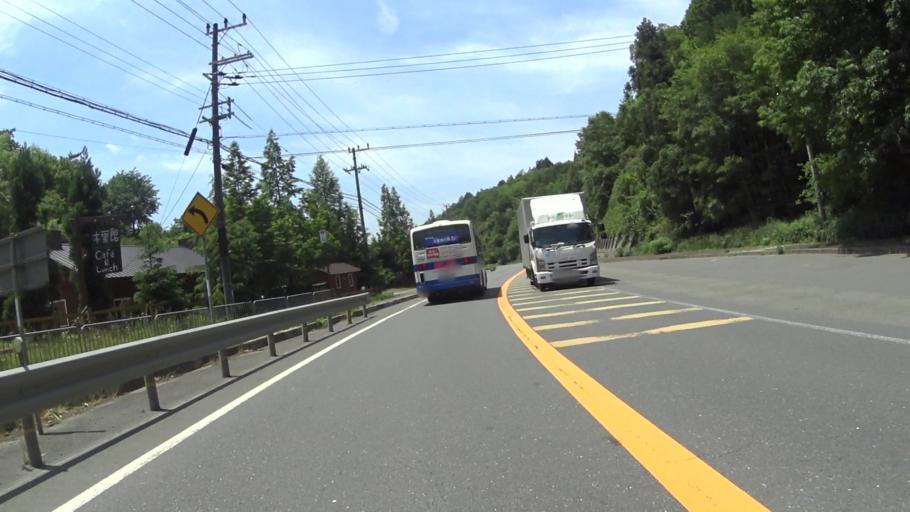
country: JP
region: Kyoto
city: Ayabe
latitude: 35.1789
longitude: 135.3534
